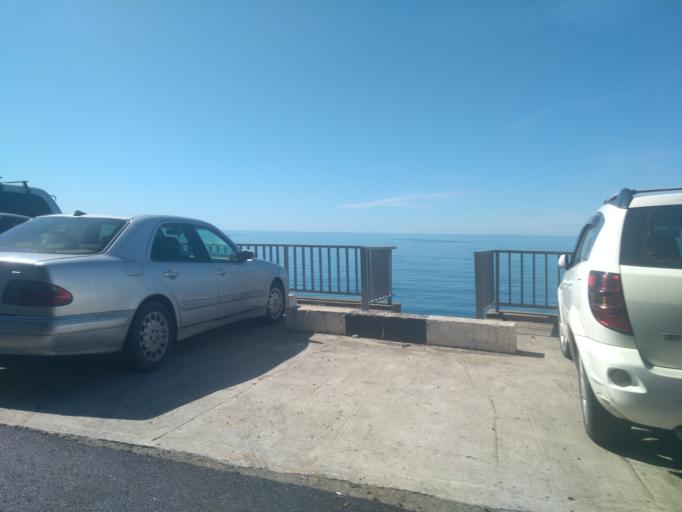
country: TR
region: Artvin
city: Kemalpasa
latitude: 41.5257
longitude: 41.5490
